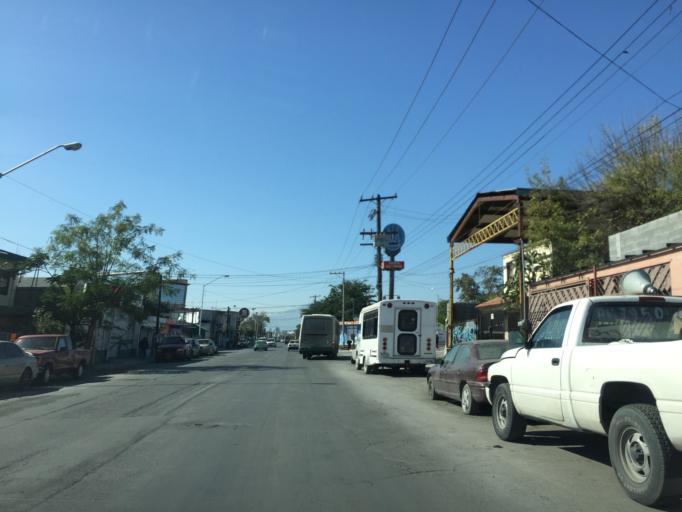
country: MX
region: Nuevo Leon
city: Guadalupe
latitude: 25.6952
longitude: -100.2204
